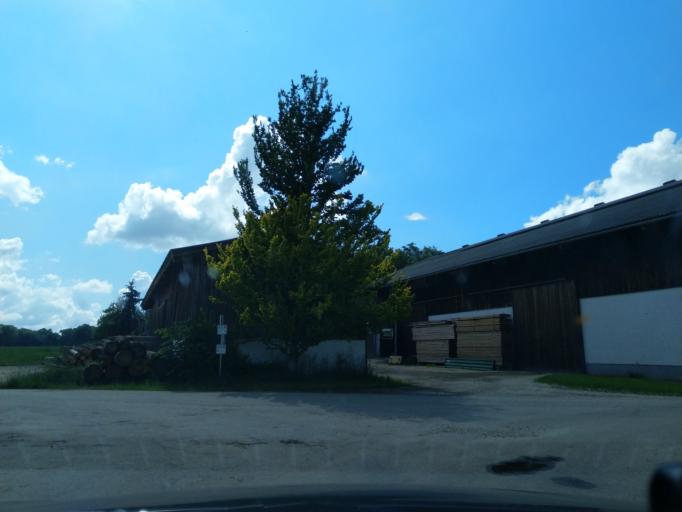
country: DE
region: Bavaria
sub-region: Lower Bavaria
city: Bad Fussing
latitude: 48.2880
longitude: 13.3139
